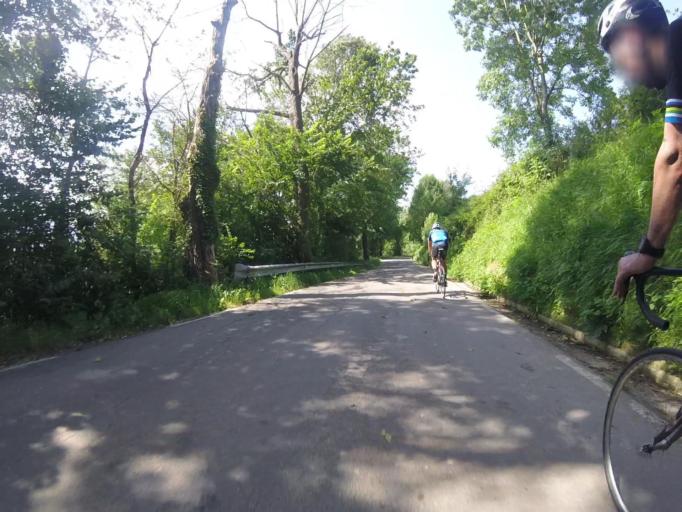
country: ES
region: Basque Country
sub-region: Provincia de Guipuzcoa
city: Orendain
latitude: 43.0801
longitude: -2.1070
